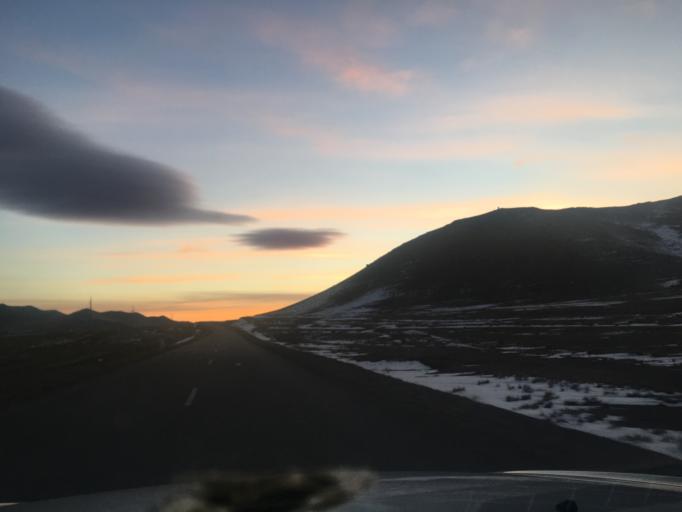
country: MN
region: Central Aimak
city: Mandal
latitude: 48.1131
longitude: 106.6396
